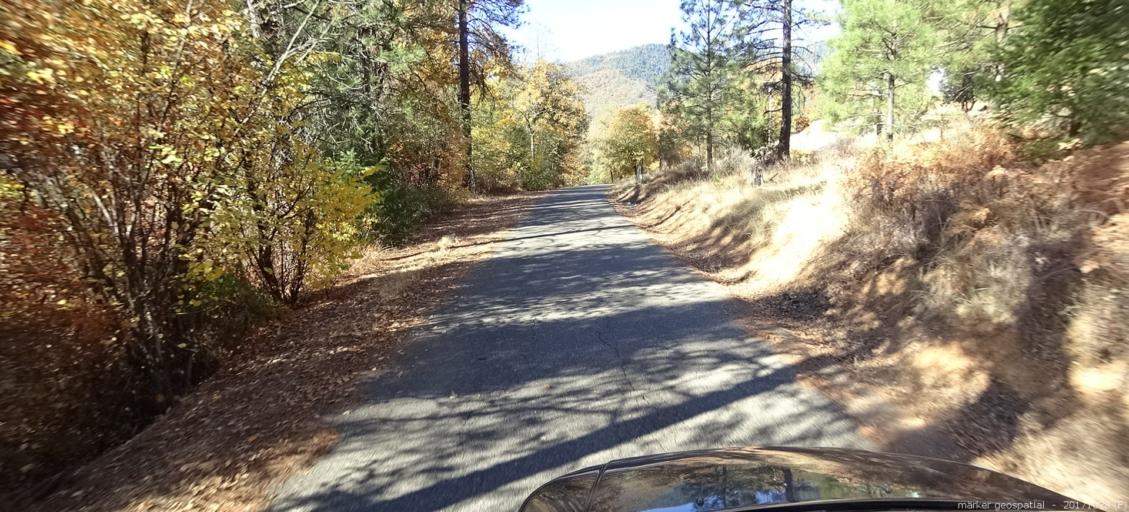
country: US
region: California
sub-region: Shasta County
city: Shasta
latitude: 40.7593
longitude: -122.5989
